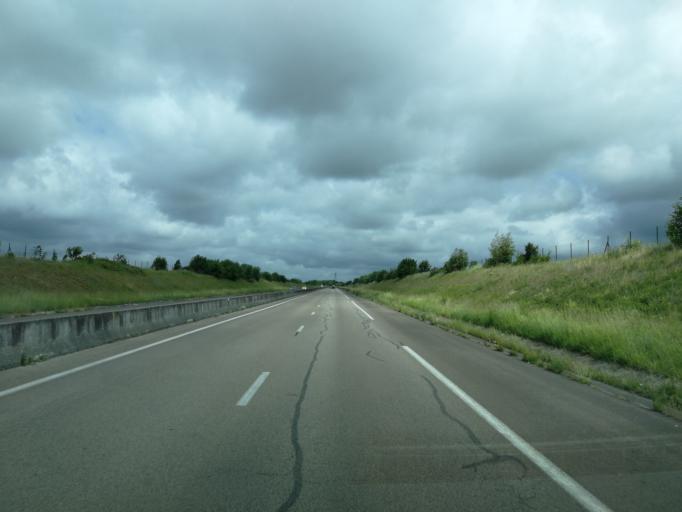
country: FR
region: Haute-Normandie
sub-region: Departement de l'Eure
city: La Madeleine-de-Nonancourt
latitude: 48.8249
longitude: 1.1899
